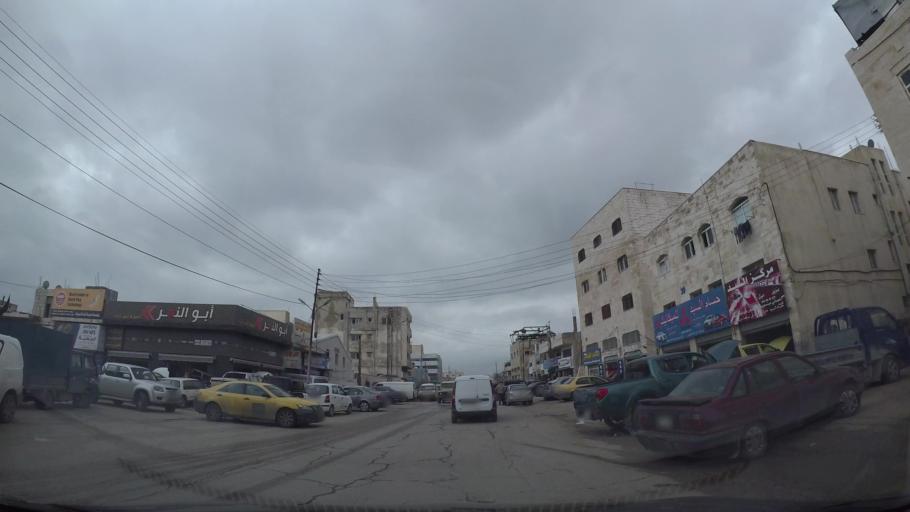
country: JO
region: Amman
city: Wadi as Sir
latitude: 31.9418
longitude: 35.8434
